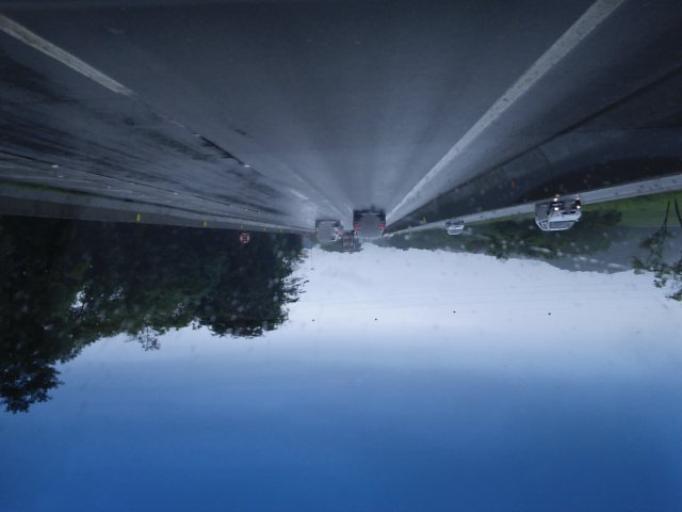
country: BR
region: Santa Catarina
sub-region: Joinville
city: Joinville
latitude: -26.0810
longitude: -48.8617
